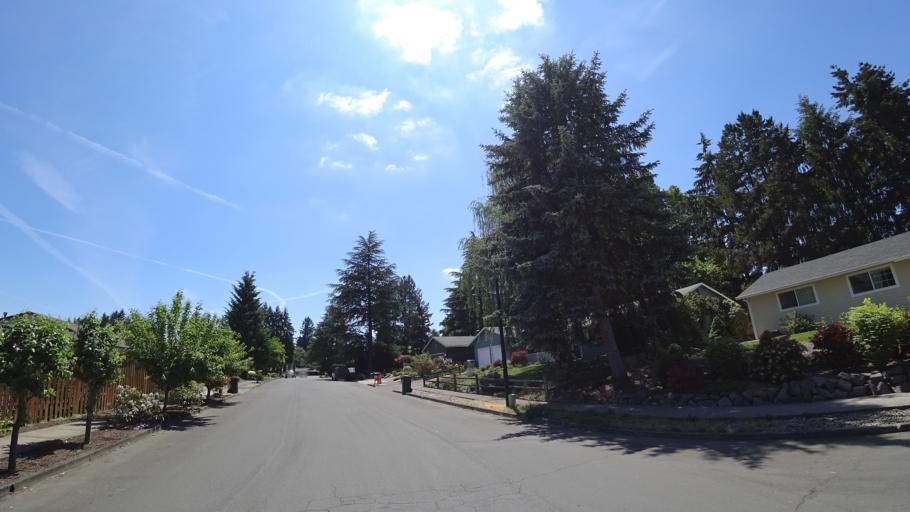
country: US
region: Oregon
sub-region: Washington County
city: King City
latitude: 45.4328
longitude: -122.8049
